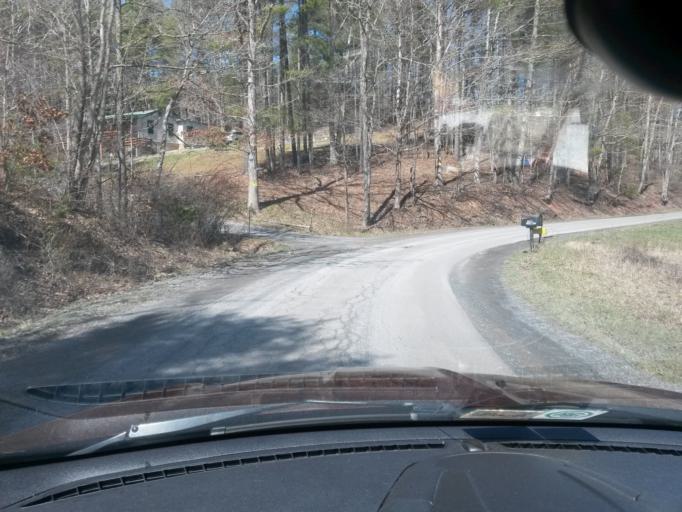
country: US
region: West Virginia
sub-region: Greenbrier County
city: White Sulphur Springs
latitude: 37.6437
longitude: -80.3319
